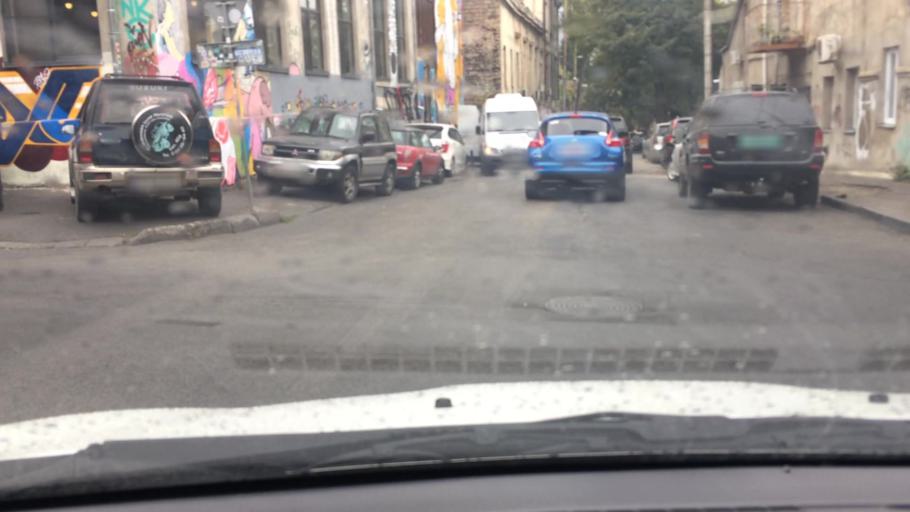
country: GE
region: T'bilisi
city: Tbilisi
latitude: 41.7102
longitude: 44.8027
